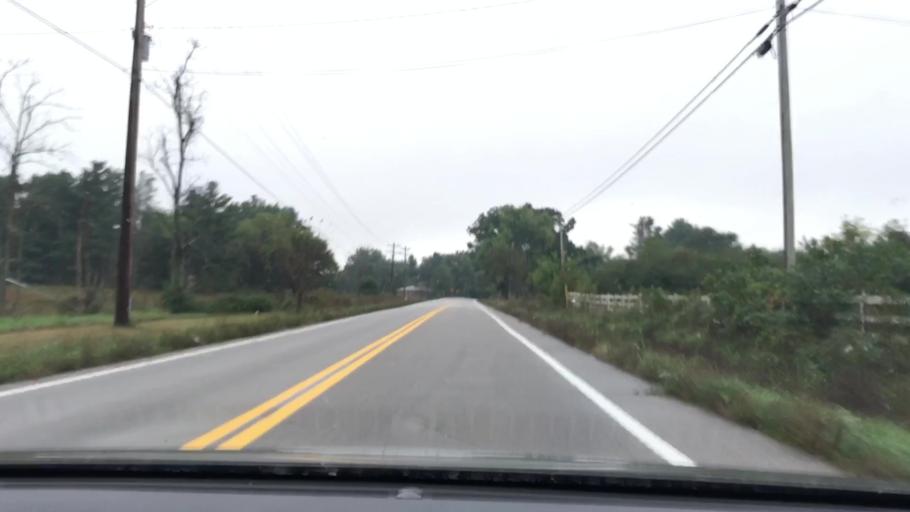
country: US
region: Tennessee
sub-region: Fentress County
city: Grimsley
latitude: 36.2012
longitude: -85.0196
